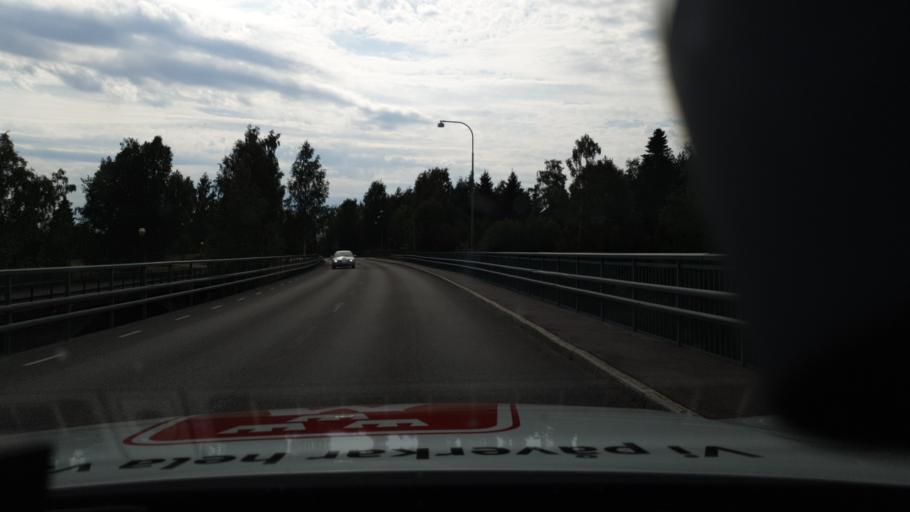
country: SE
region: Norrbotten
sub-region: Lulea Kommun
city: Ranea
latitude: 65.8554
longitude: 22.2835
